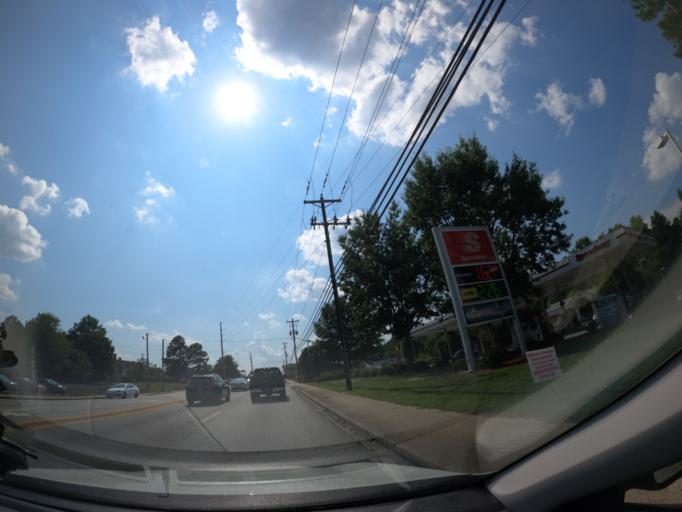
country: US
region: South Carolina
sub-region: Lexington County
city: Springdale
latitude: 33.9787
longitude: -81.1173
